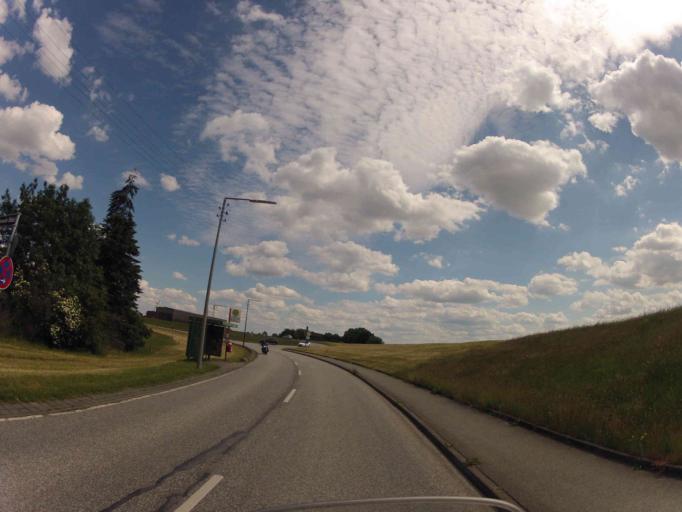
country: DE
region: Lower Saxony
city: Stelle
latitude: 53.4490
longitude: 10.0904
